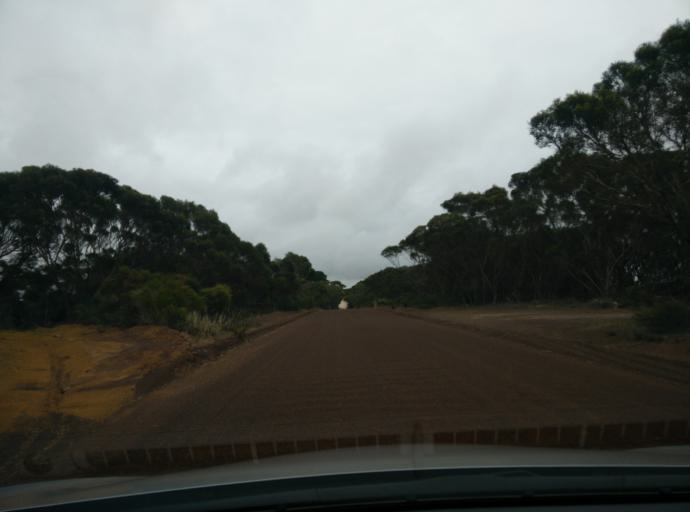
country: AU
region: South Australia
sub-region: Kangaroo Island
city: Kingscote
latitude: -35.8531
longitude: 137.4788
